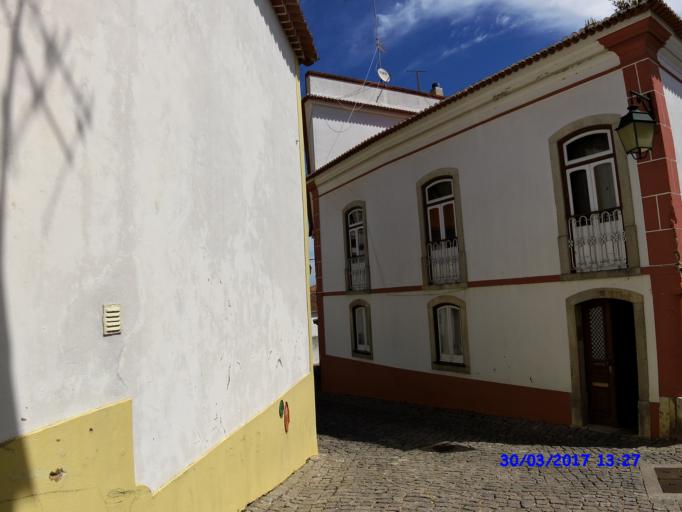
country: PT
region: Faro
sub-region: Monchique
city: Monchique
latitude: 37.3189
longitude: -8.5571
